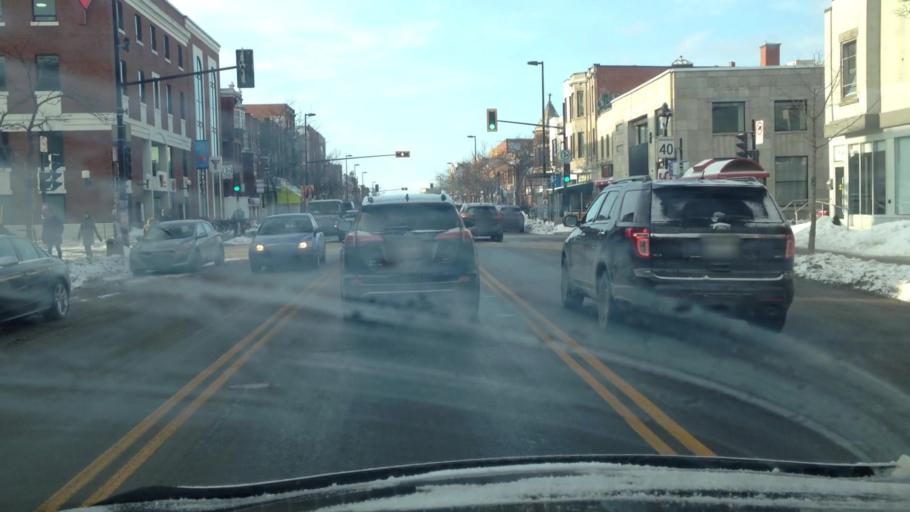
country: CA
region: Quebec
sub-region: Montreal
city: Montreal
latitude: 45.5220
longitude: -73.6016
